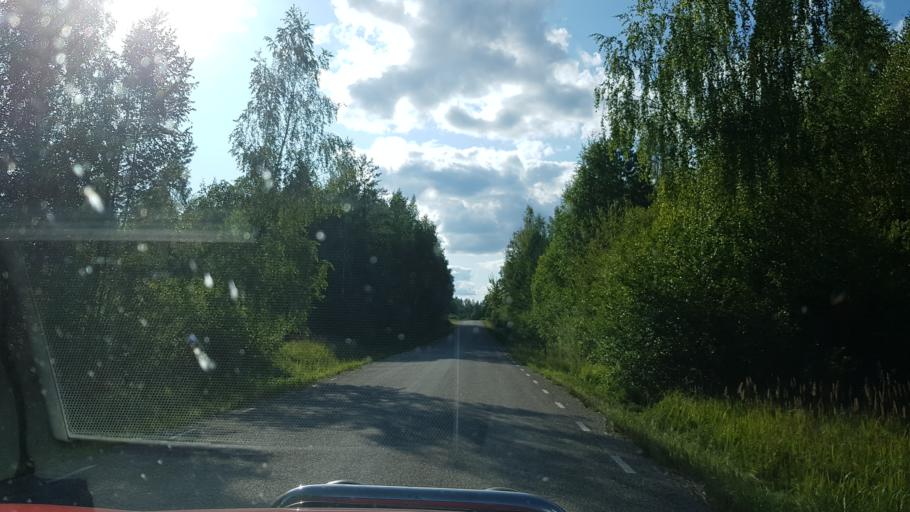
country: EE
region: Vorumaa
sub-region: Voru linn
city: Voru
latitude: 57.9279
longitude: 27.0642
